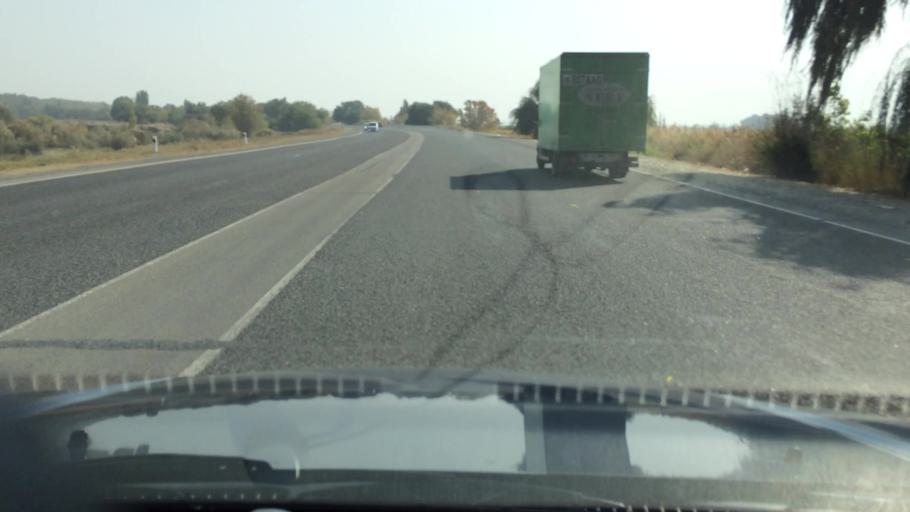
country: KG
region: Chuy
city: Kant
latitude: 42.9416
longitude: 74.9675
